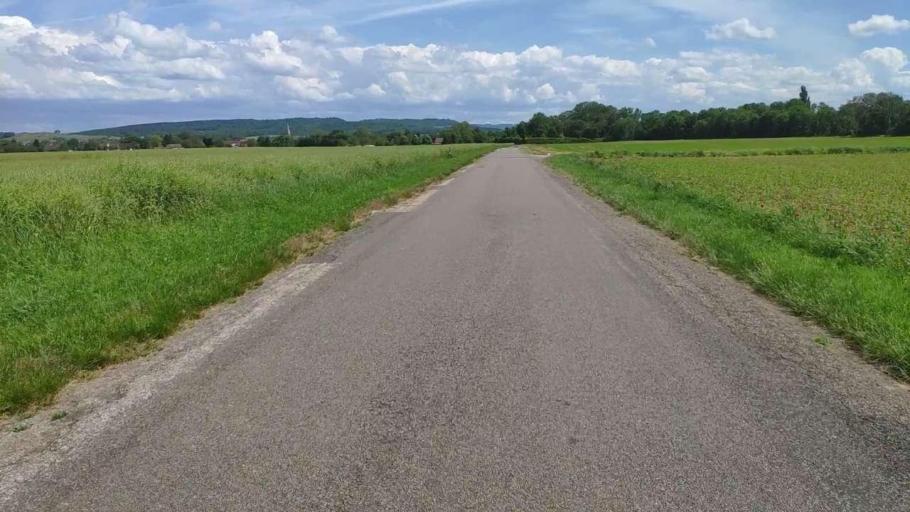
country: FR
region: Franche-Comte
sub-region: Departement du Jura
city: Bletterans
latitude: 46.7487
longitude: 5.4797
